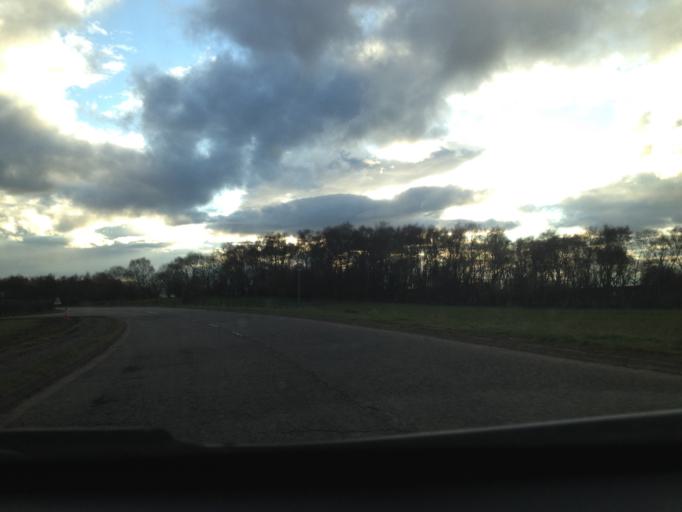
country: GB
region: Scotland
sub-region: South Lanarkshire
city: Law
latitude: 55.7467
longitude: -3.8945
